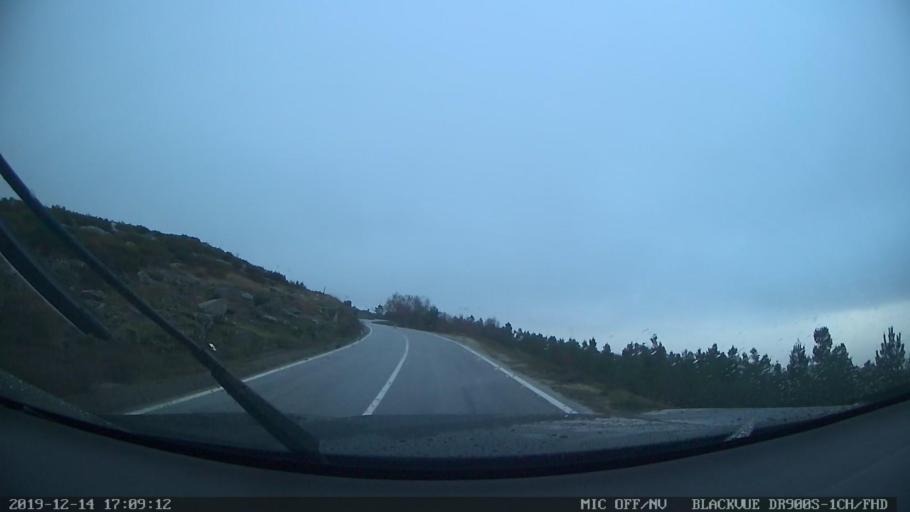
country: PT
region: Vila Real
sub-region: Vila Pouca de Aguiar
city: Vila Pouca de Aguiar
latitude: 41.4744
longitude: -7.6036
